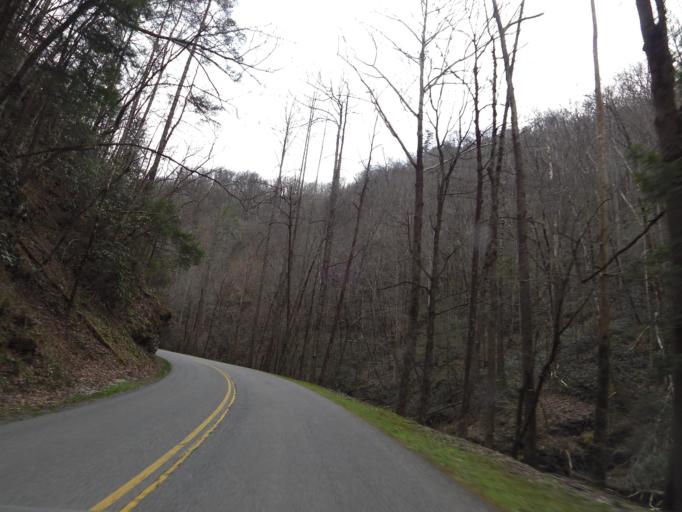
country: US
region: Tennessee
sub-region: Sevier County
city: Pigeon Forge
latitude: 35.6477
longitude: -83.7183
